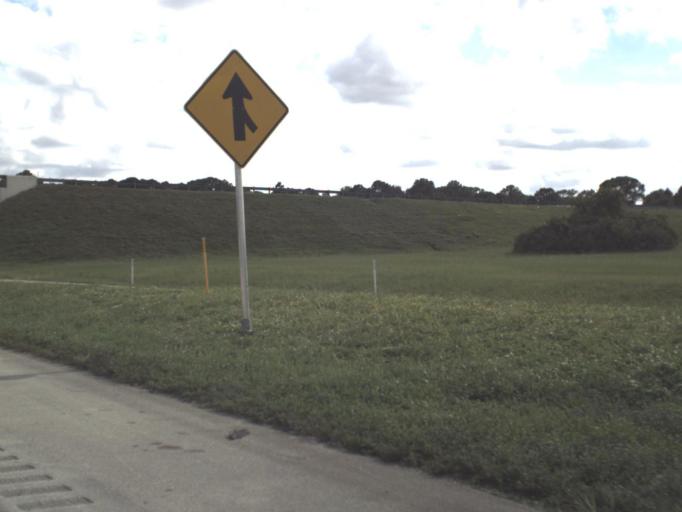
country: US
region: Florida
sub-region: Saint Lucie County
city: Port Saint Lucie
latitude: 27.2771
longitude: -80.3606
